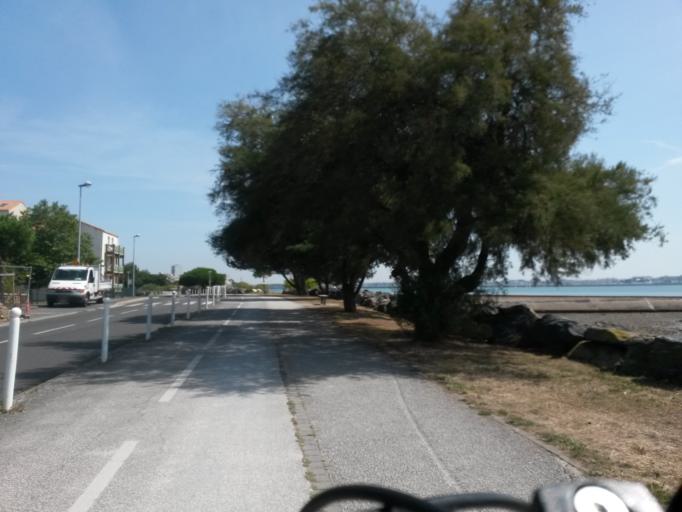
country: FR
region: Poitou-Charentes
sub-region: Departement de la Charente-Maritime
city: La Rochelle
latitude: 46.1537
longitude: -1.1856
